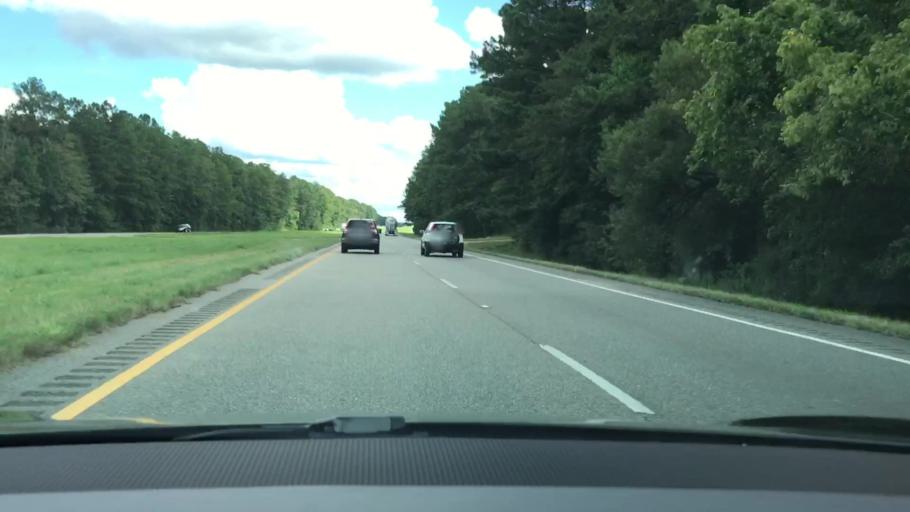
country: US
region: Alabama
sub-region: Montgomery County
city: Pike Road
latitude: 32.1359
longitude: -86.0900
